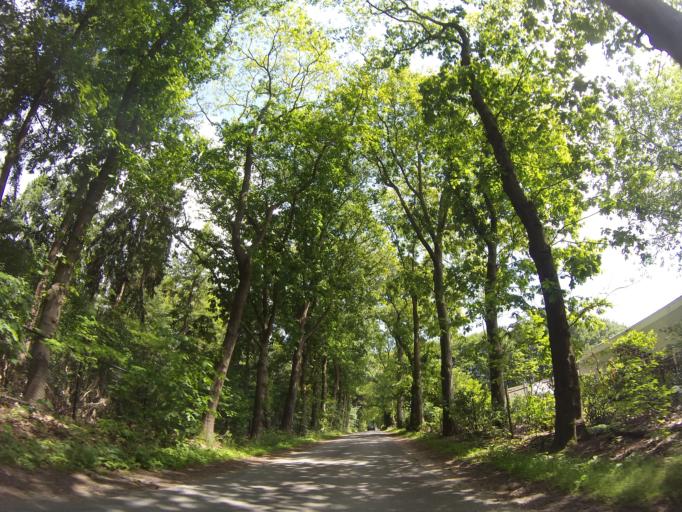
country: NL
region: Gelderland
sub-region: Gemeente Barneveld
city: Stroe
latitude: 52.2101
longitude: 5.6500
